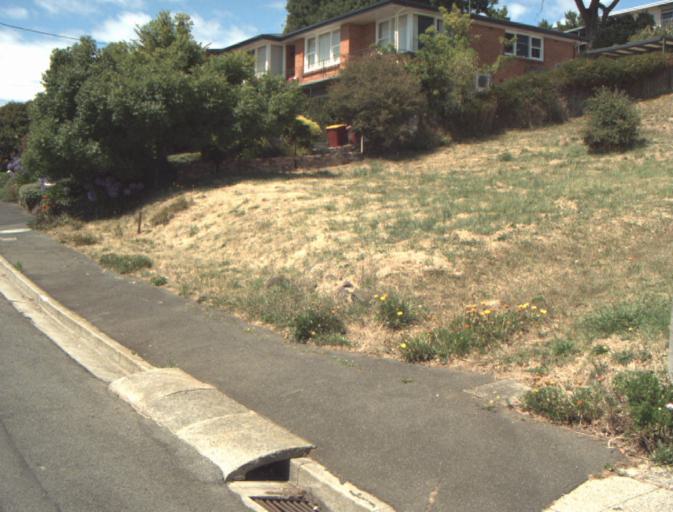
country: AU
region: Tasmania
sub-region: Launceston
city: West Launceston
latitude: -41.4594
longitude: 147.1342
